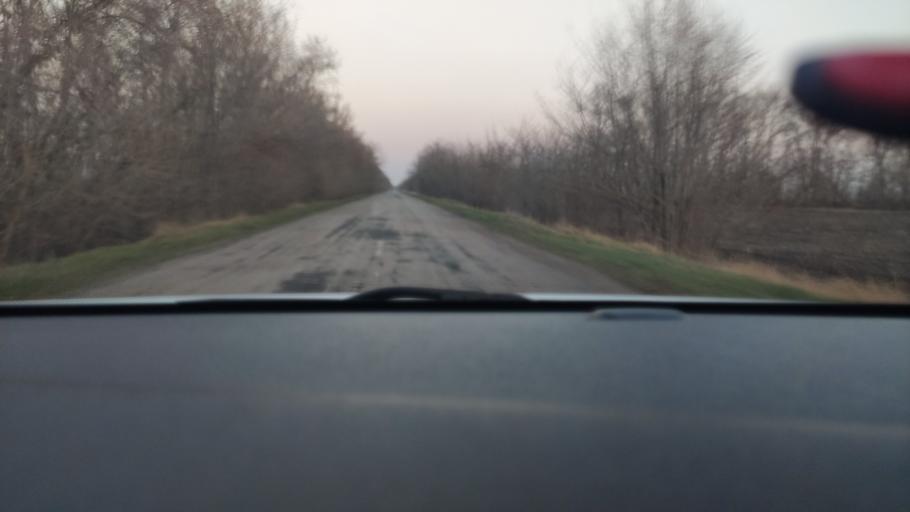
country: RU
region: Voronezj
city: Uryv-Pokrovka
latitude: 51.1388
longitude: 39.0808
